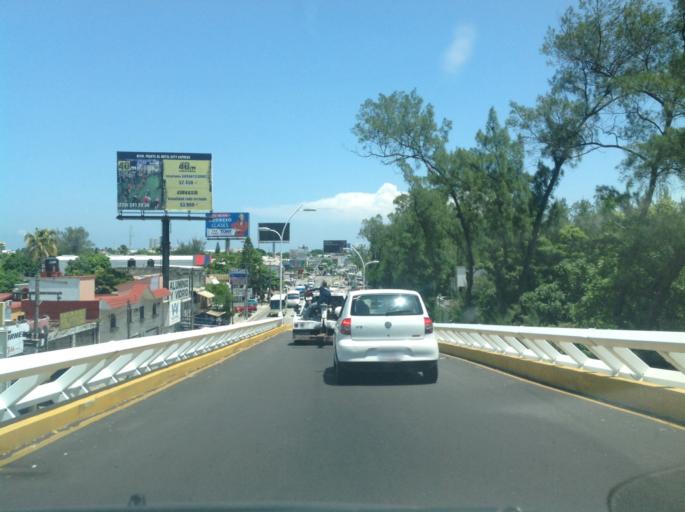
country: MX
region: Veracruz
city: Veracruz
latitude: 19.1461
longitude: -96.1284
